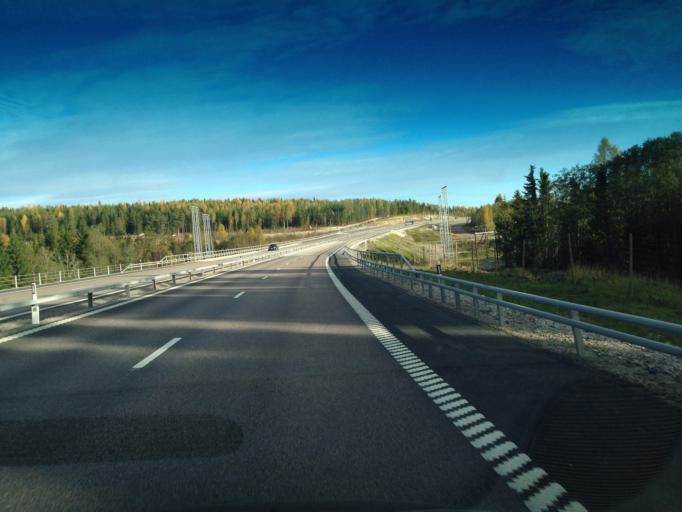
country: SE
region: Vaesternorrland
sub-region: Sundsvalls Kommun
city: Stockvik
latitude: 62.3326
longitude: 17.3452
